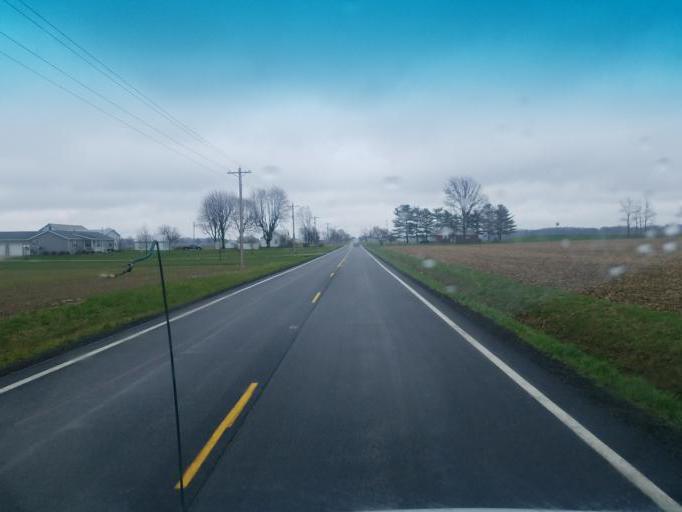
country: US
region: Ohio
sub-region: Huron County
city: Willard
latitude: 40.9601
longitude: -82.7787
